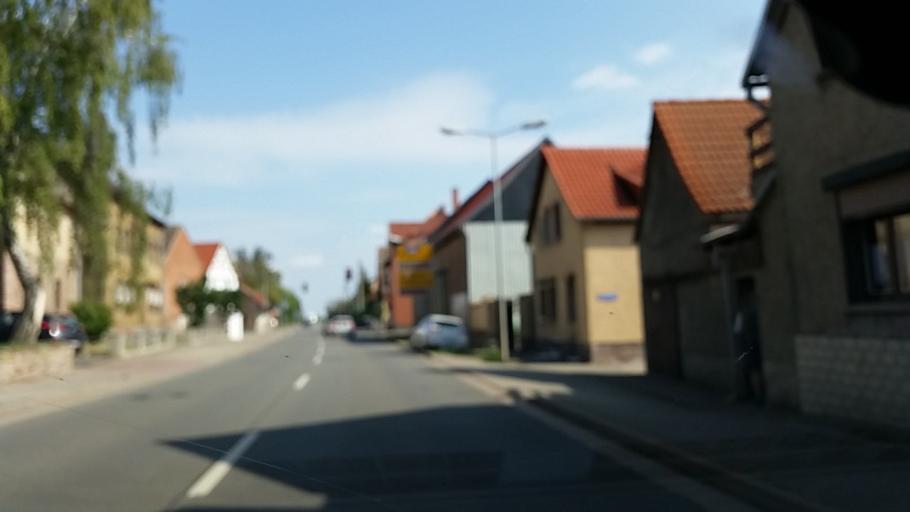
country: DE
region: Thuringia
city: Oldisleben
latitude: 51.3475
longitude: 11.1787
